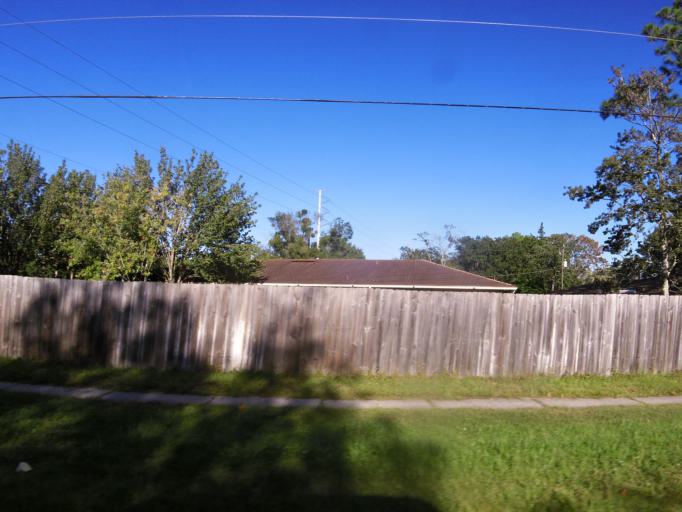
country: US
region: Florida
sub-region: Duval County
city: Neptune Beach
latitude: 30.3029
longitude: -81.4438
